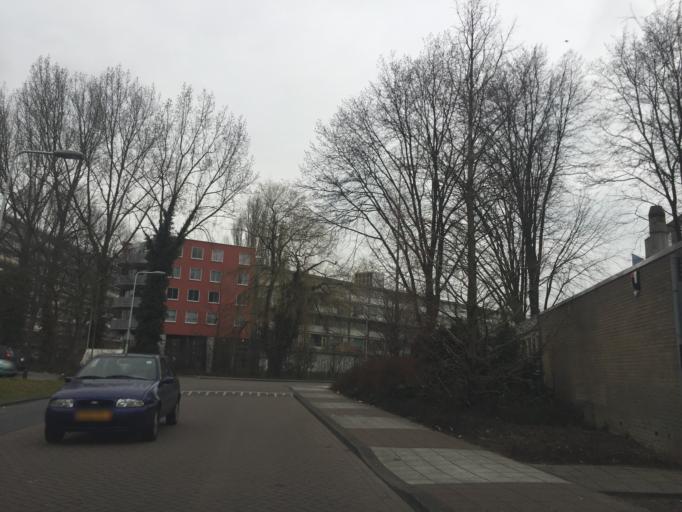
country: NL
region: South Holland
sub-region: Gemeente Leiden
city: Leiden
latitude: 52.1735
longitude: 4.5053
